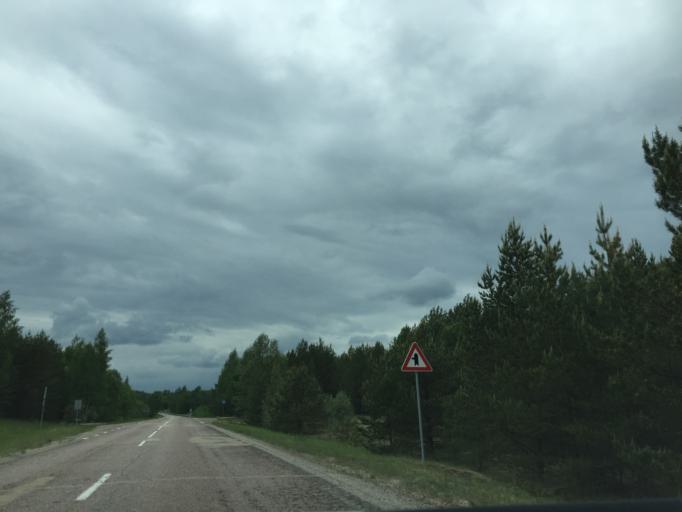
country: LV
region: Aglona
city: Aglona
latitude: 56.1483
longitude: 27.1744
